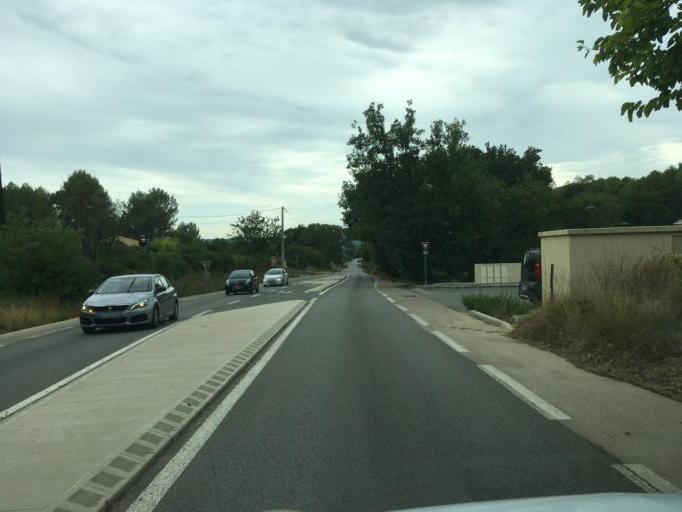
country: FR
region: Provence-Alpes-Cote d'Azur
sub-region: Departement des Bouches-du-Rhone
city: Rousset
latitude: 43.4884
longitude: 5.6294
